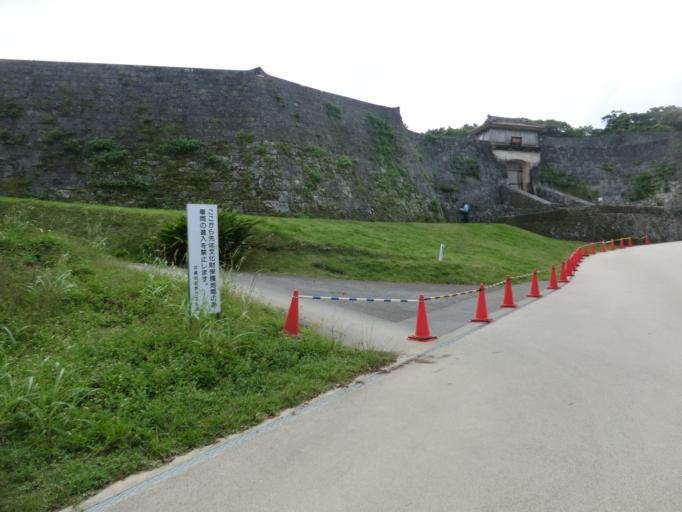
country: JP
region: Okinawa
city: Naha-shi
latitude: 26.2182
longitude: 127.7187
